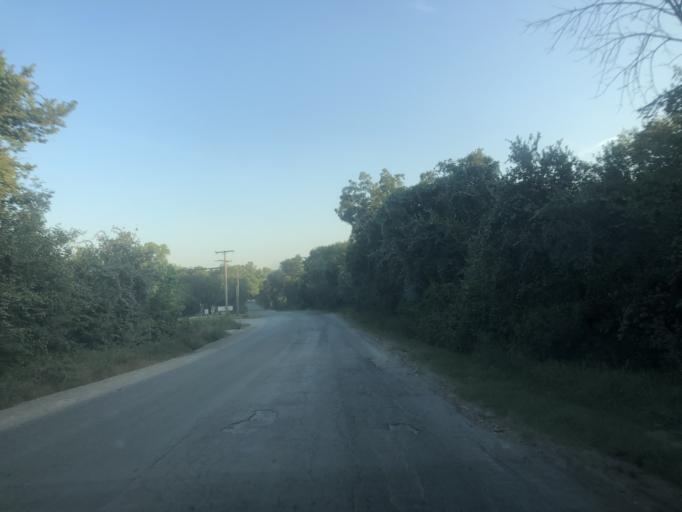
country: US
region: Texas
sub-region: Tarrant County
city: Lakeside
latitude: 32.7909
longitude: -97.4913
